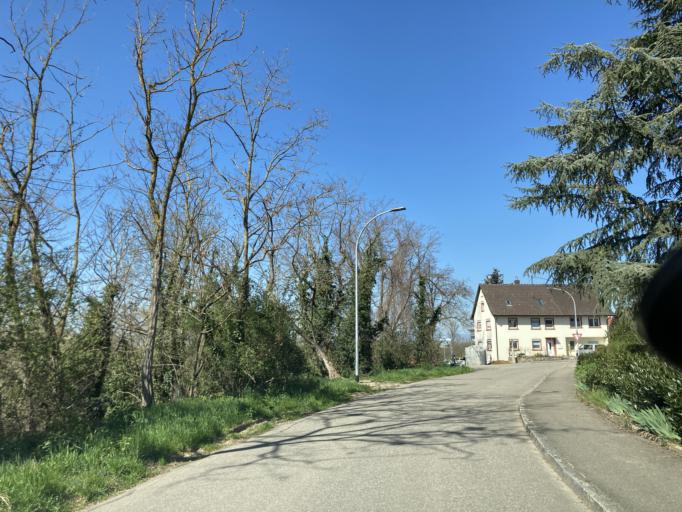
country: DE
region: Baden-Wuerttemberg
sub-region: Freiburg Region
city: Schliengen
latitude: 47.7643
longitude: 7.5551
